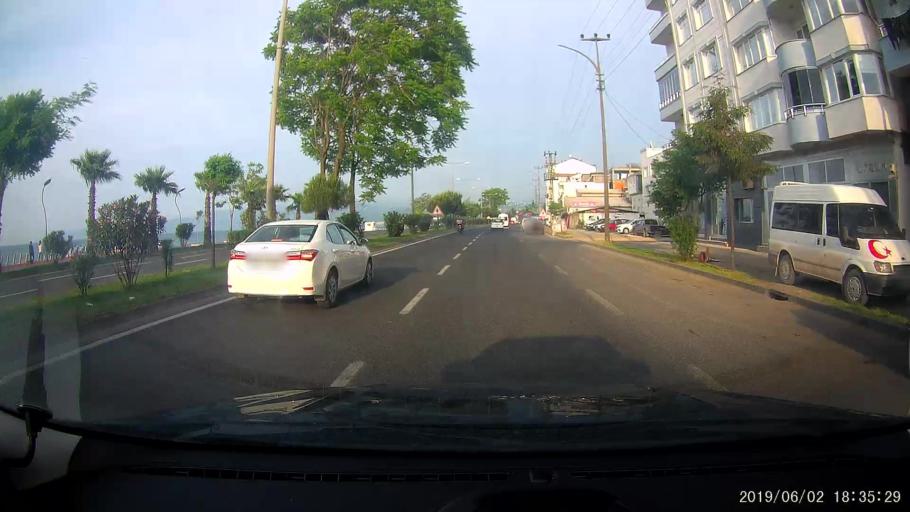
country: TR
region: Ordu
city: Fatsa
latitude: 41.0263
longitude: 37.5170
